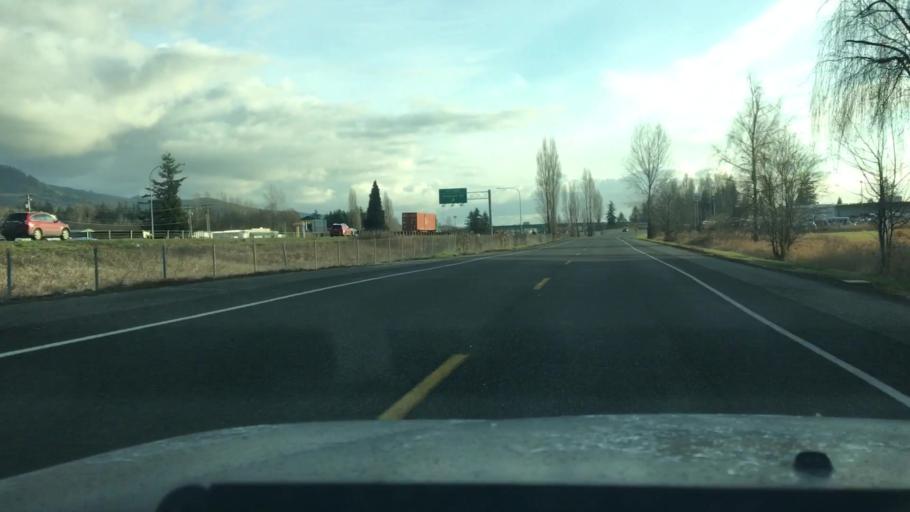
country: US
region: Washington
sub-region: Skagit County
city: Mount Vernon
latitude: 48.4047
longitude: -122.3314
